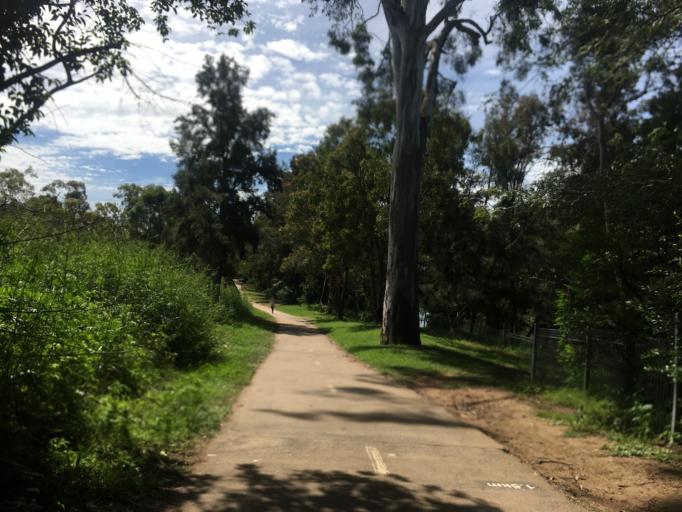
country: AU
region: New South Wales
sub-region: Camden
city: Elderslie
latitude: -34.0664
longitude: 150.6991
